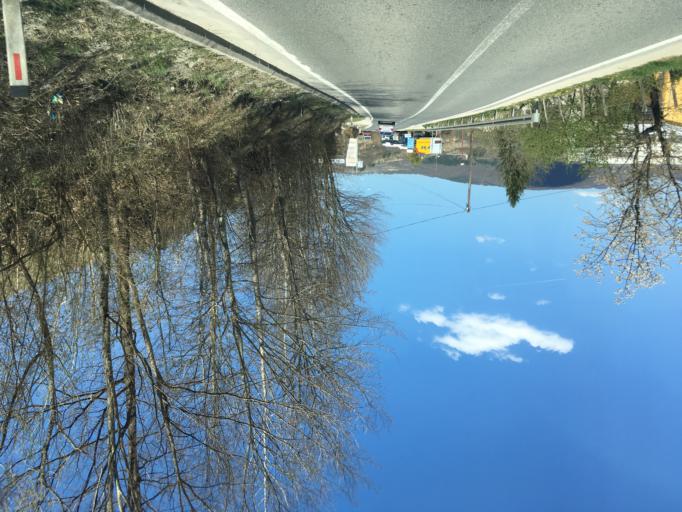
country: BA
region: Federation of Bosnia and Herzegovina
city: Jajce
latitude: 44.3513
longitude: 17.2985
